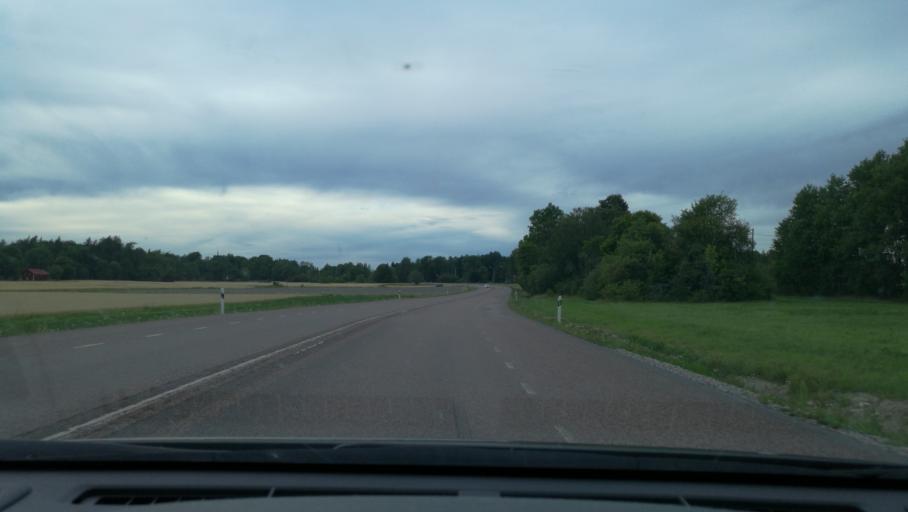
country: SE
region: Vaestmanland
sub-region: Kungsors Kommun
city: Kungsoer
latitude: 59.4432
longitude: 16.0458
